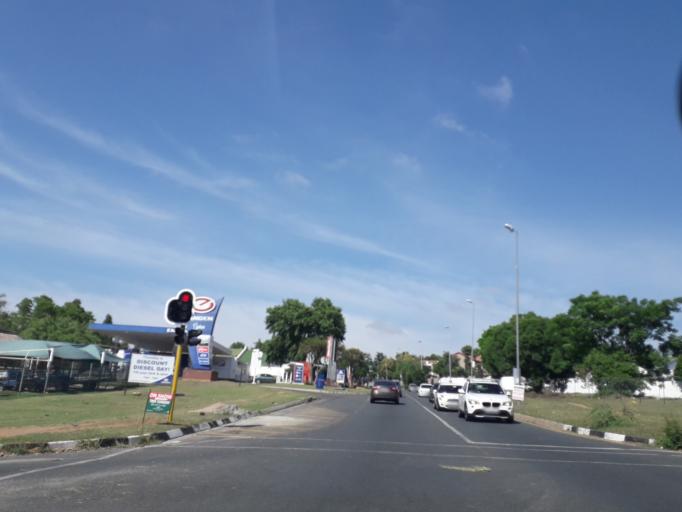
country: ZA
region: Gauteng
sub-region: City of Johannesburg Metropolitan Municipality
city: Roodepoort
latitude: -26.0721
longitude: 27.9648
